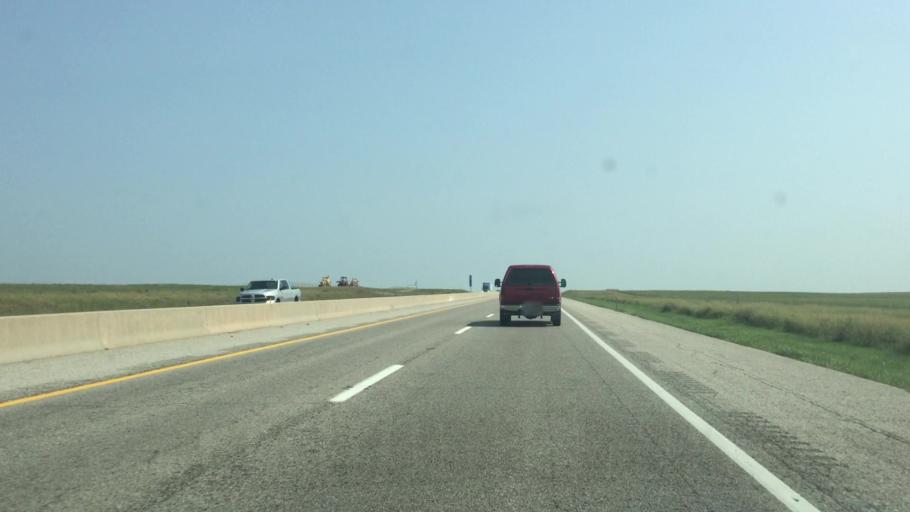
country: US
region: Kansas
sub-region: Lyon County
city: Emporia
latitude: 38.2967
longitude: -96.3522
